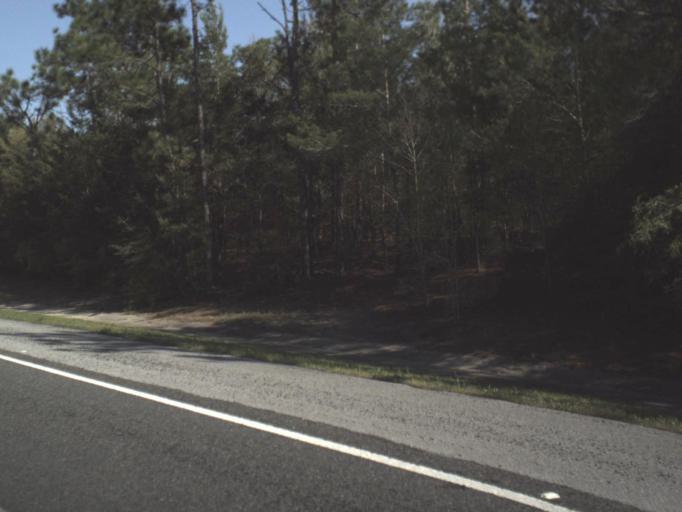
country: US
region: Florida
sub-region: Okaloosa County
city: Crestview
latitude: 30.7268
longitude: -86.5115
